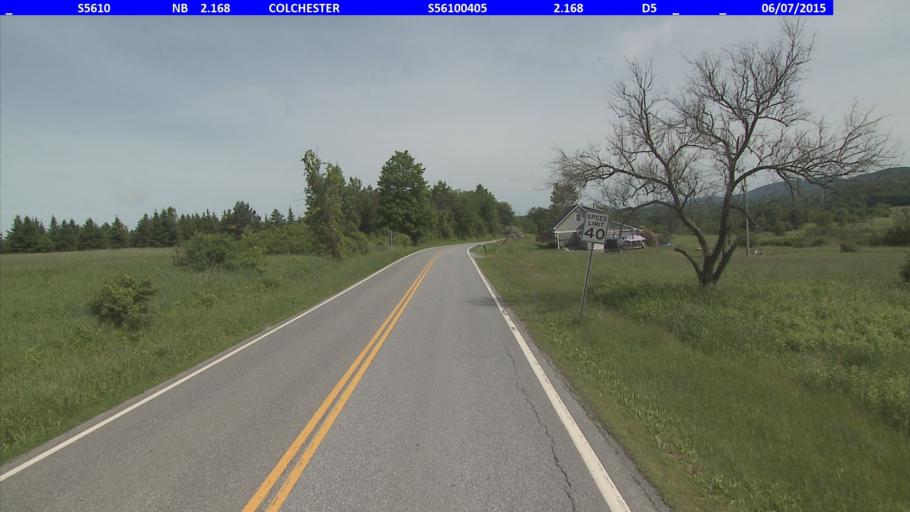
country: US
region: Vermont
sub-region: Chittenden County
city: Colchester
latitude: 44.5707
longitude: -73.1274
